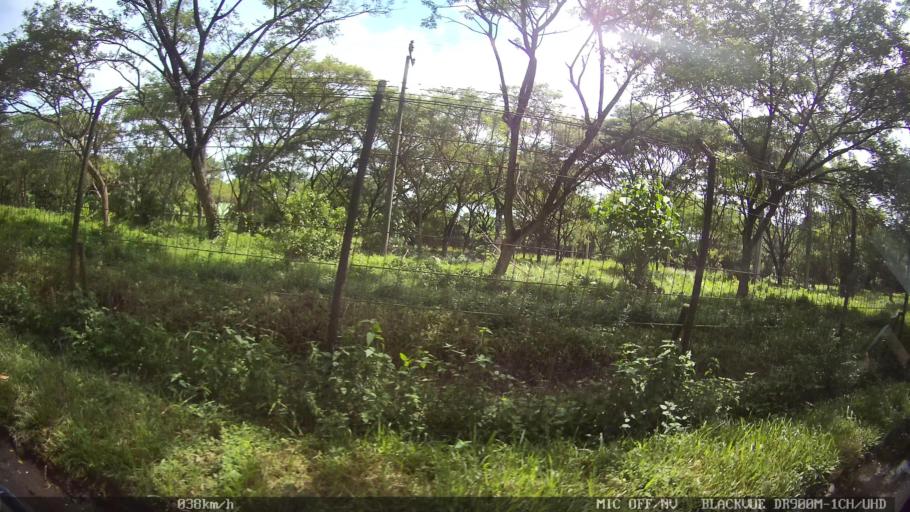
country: ID
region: North Sumatra
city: Percut
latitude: 3.6072
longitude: 98.8577
